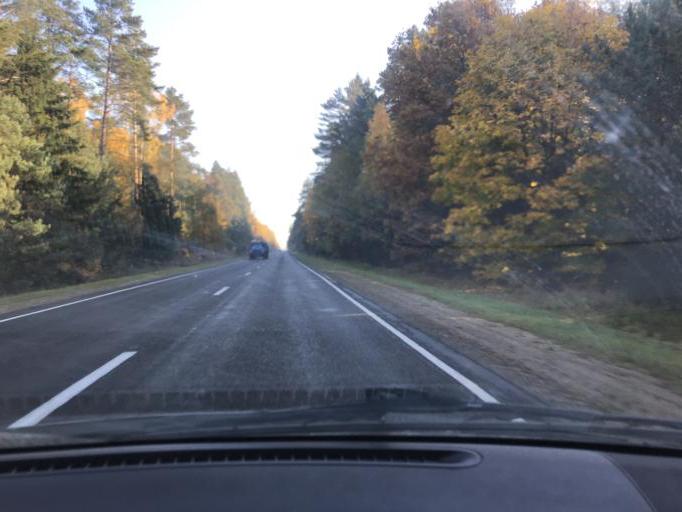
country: BY
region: Brest
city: Lyakhavichy
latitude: 52.9527
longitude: 26.2201
